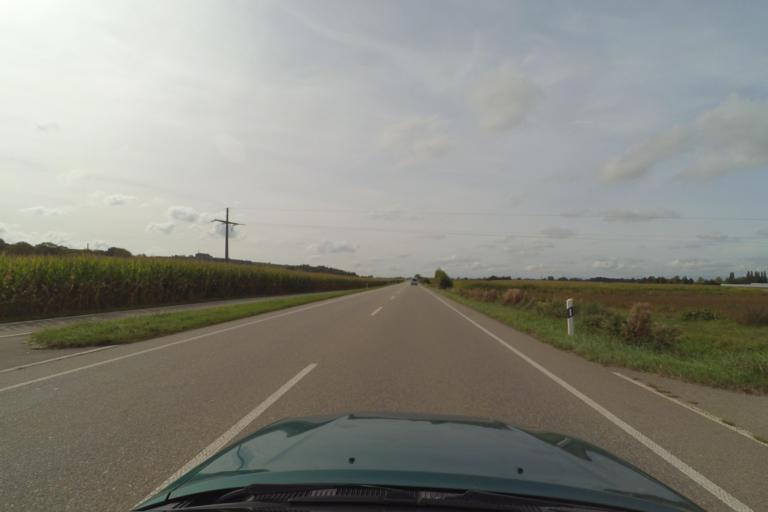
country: DE
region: Baden-Wuerttemberg
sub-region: Freiburg Region
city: Friesenheim
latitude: 48.3681
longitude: 7.8680
